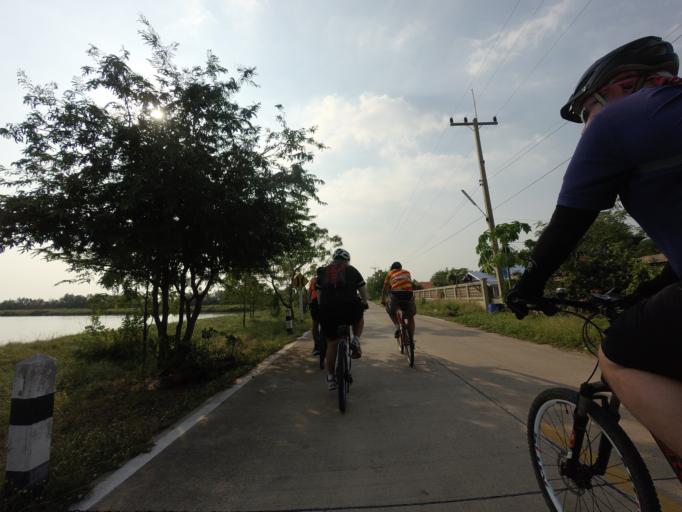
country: TH
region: Samut Sakhon
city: Samut Sakhon
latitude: 13.5080
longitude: 100.3177
